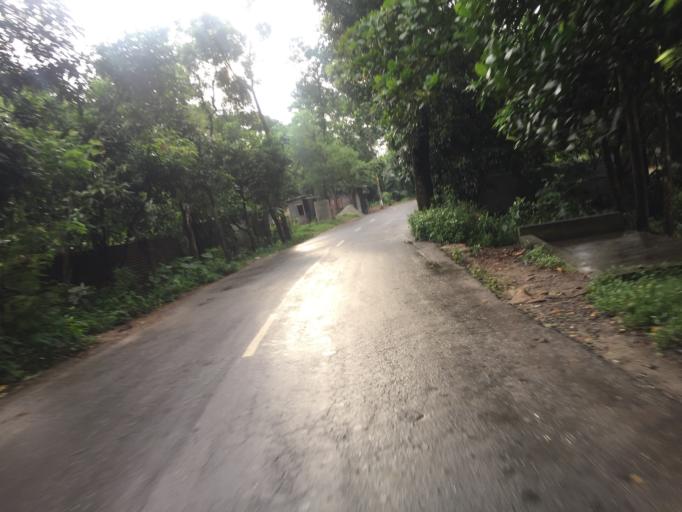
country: BD
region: Dhaka
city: Narayanganj
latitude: 23.5439
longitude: 90.4746
